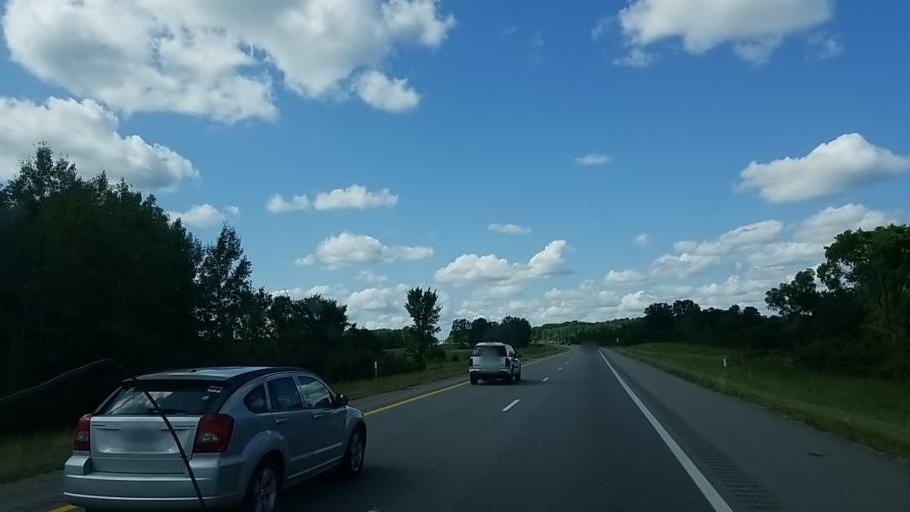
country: US
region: Michigan
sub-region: Mecosta County
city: Big Rapids
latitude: 43.6197
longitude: -85.4977
